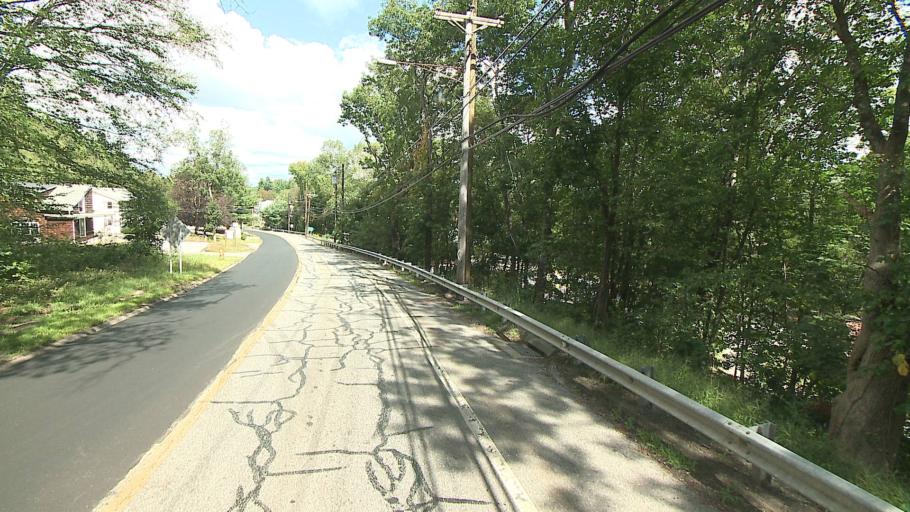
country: US
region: Connecticut
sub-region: Windham County
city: Putnam
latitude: 41.9090
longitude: -71.9145
